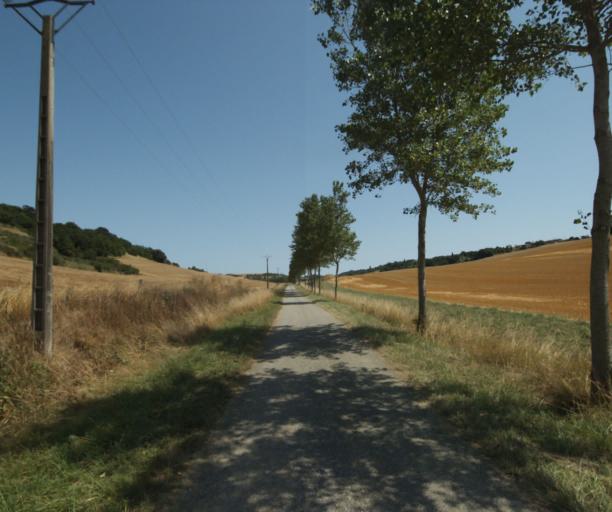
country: FR
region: Midi-Pyrenees
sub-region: Departement de la Haute-Garonne
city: Saint-Felix-Lauragais
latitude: 43.4618
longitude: 1.8637
